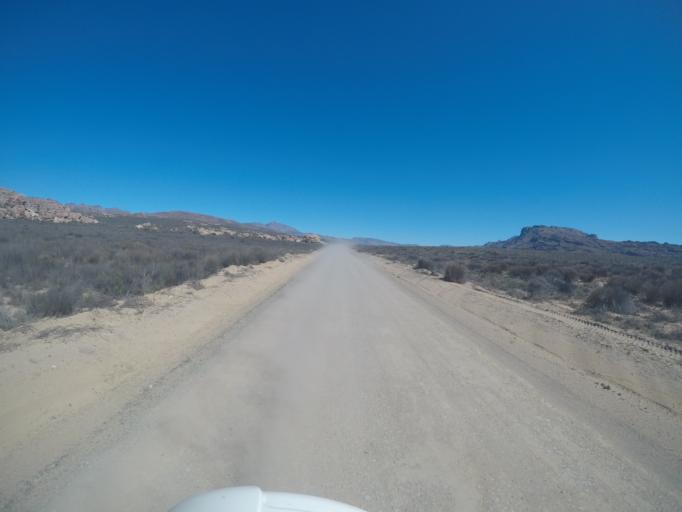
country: ZA
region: Western Cape
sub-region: West Coast District Municipality
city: Clanwilliam
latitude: -32.5101
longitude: 19.3140
